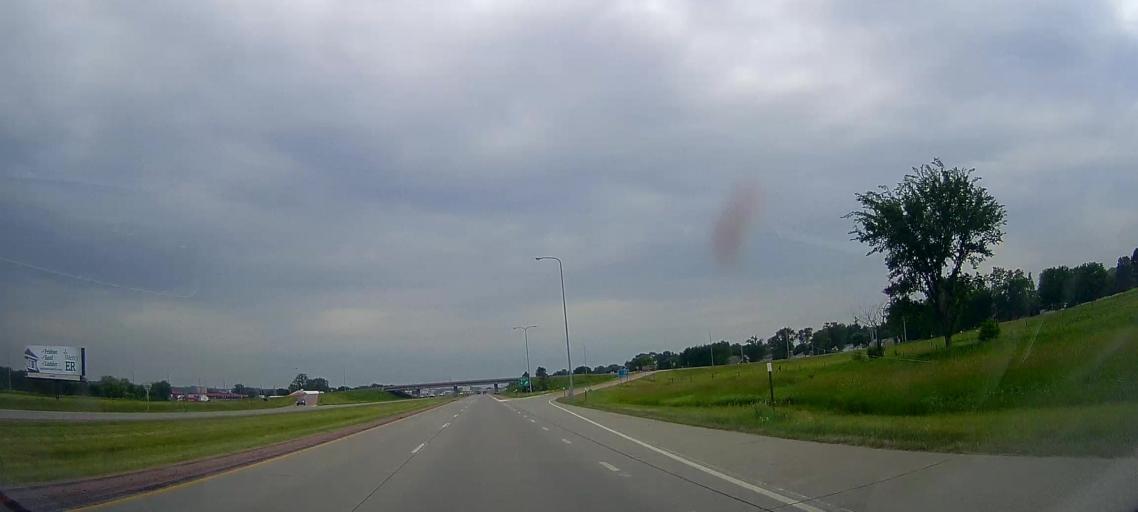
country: US
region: South Dakota
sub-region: Union County
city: North Sioux City
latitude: 42.5526
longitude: -96.5111
